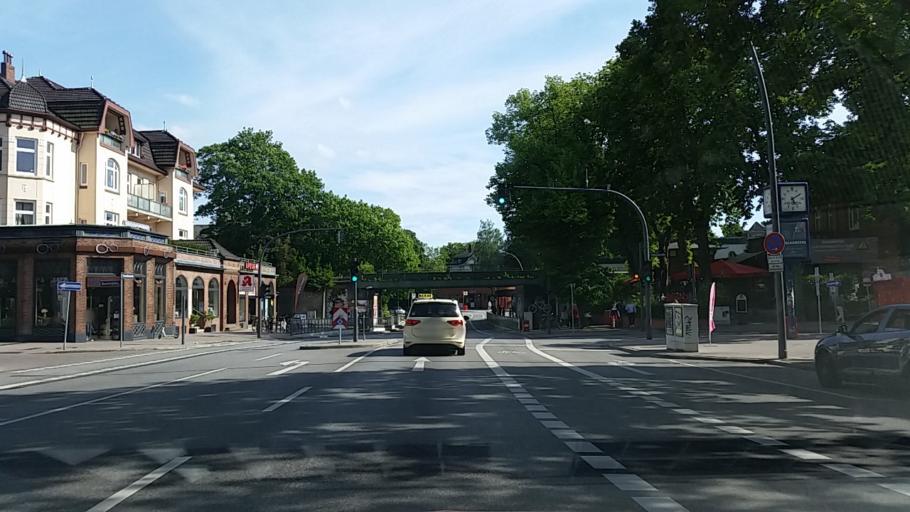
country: DE
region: Hamburg
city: Altona
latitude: 53.5600
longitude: 9.8871
